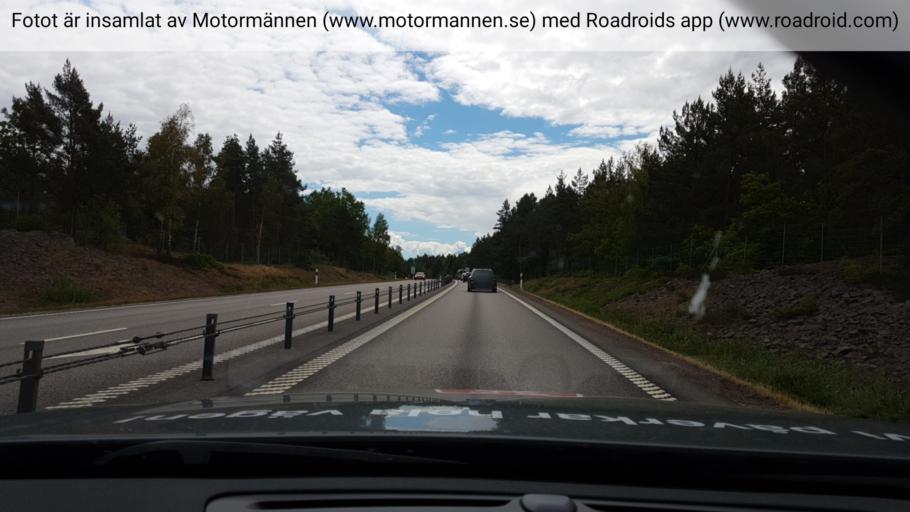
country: SE
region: Kalmar
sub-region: Oskarshamns Kommun
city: Paskallavik
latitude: 57.1373
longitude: 16.4716
